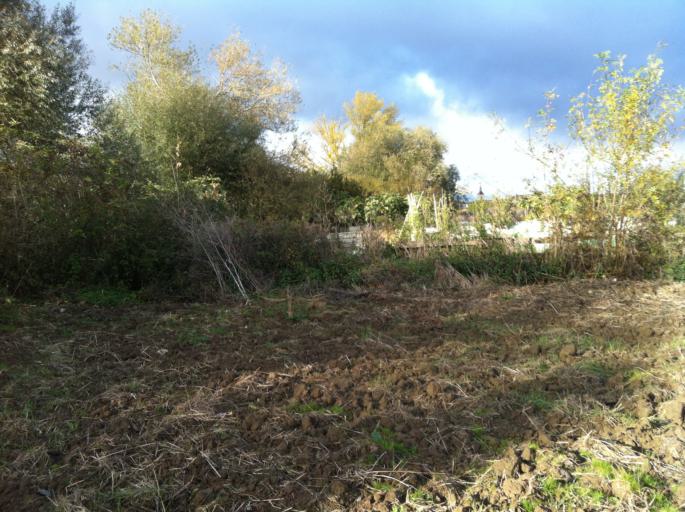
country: ES
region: Basque Country
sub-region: Provincia de Alava
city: Gasteiz / Vitoria
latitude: 42.8566
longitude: -2.7326
